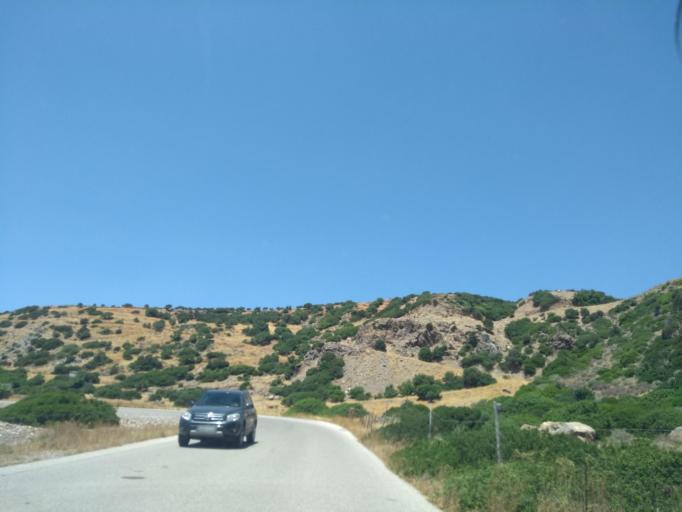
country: GR
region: Crete
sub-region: Nomos Chanias
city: Vryses
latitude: 35.3516
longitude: 23.5370
